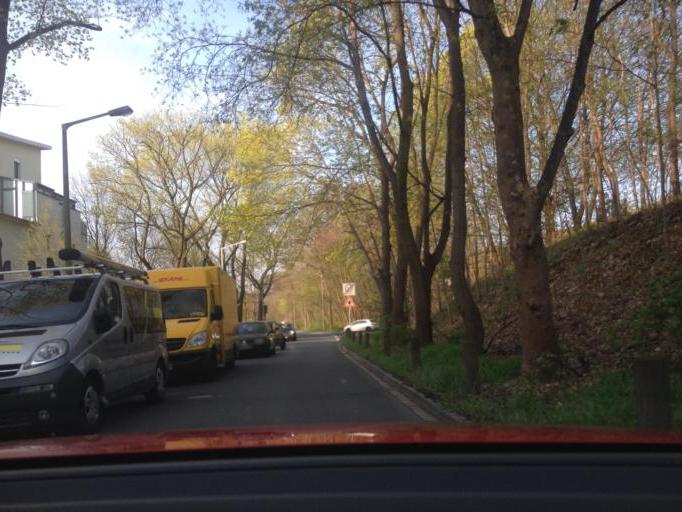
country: DE
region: Bavaria
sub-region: Regierungsbezirk Mittelfranken
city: Nuernberg
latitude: 49.4615
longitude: 11.1169
